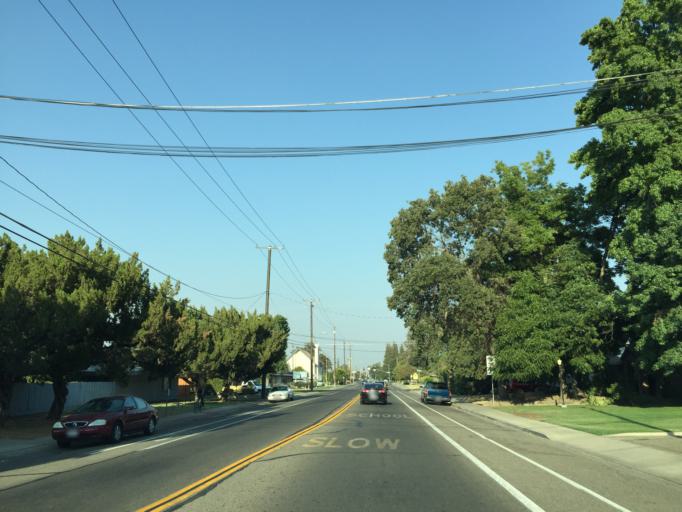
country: US
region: California
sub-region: Tulare County
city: Visalia
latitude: 36.3200
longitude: -119.3045
